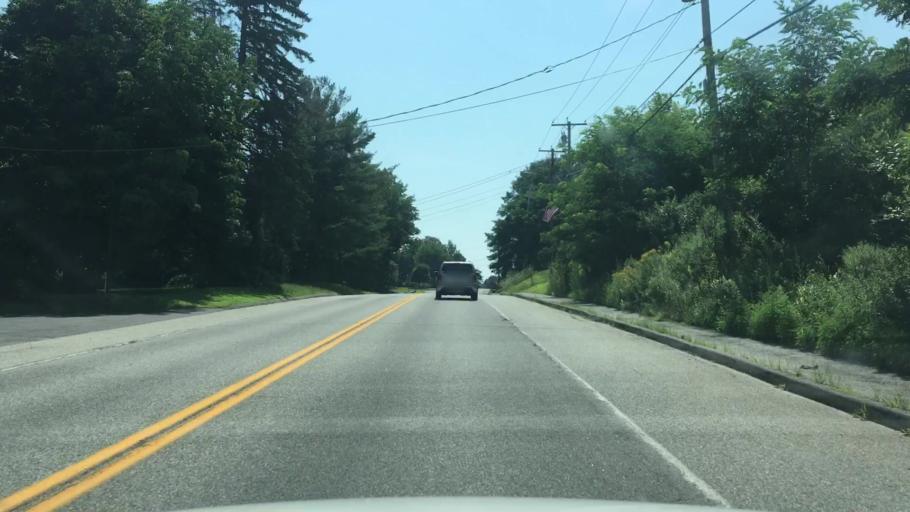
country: US
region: Maine
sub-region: Kennebec County
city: Hallowell
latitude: 44.2665
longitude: -69.7859
